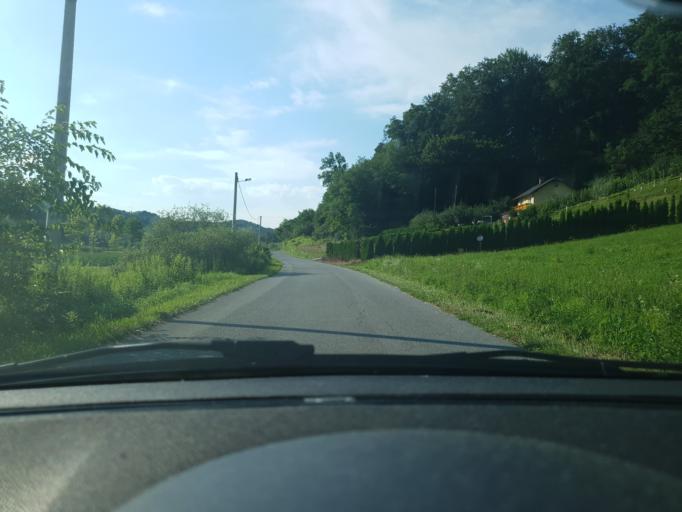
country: HR
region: Krapinsko-Zagorska
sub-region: Grad Krapina
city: Krapina
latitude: 46.1354
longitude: 15.8557
